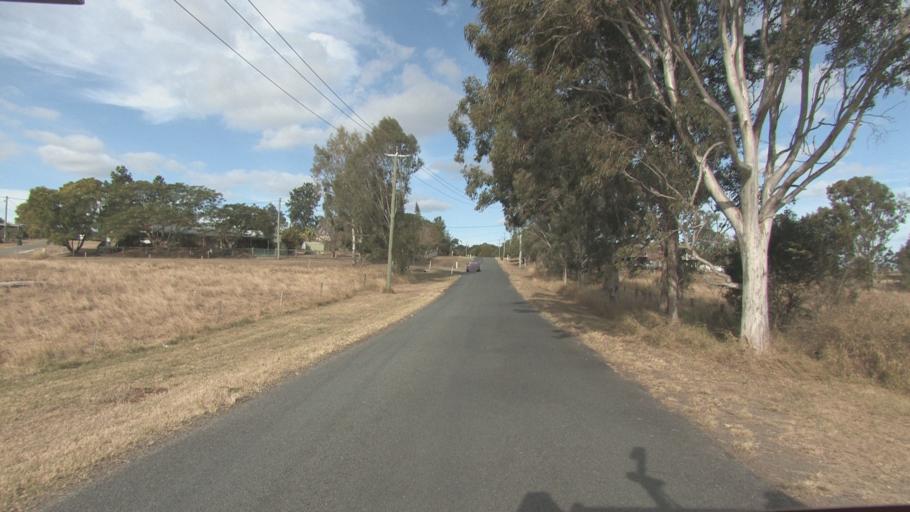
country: AU
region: Queensland
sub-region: Logan
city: Cedar Vale
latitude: -27.9126
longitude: 152.9860
